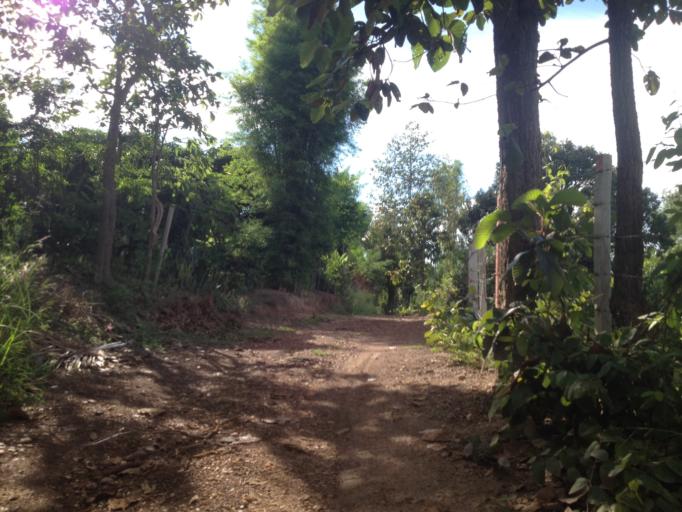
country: TH
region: Chiang Mai
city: Hang Dong
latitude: 18.7029
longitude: 98.8914
